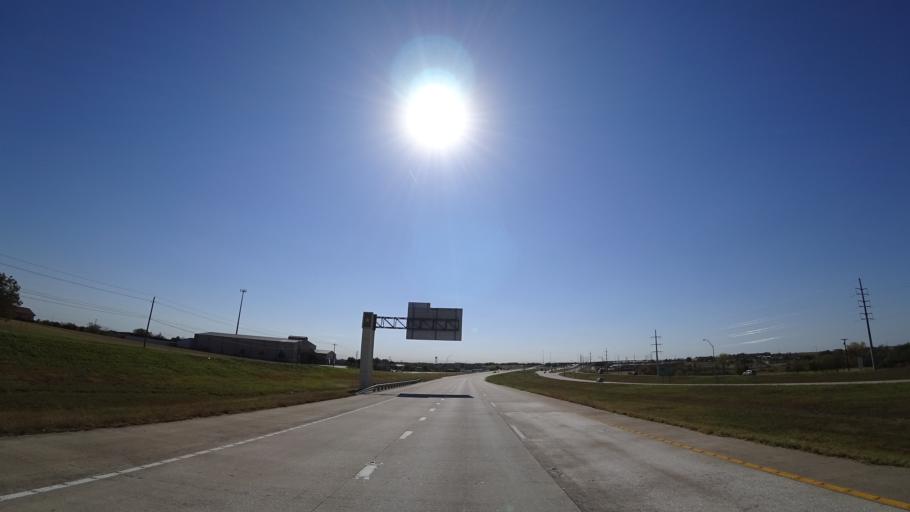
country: US
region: Texas
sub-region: Travis County
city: Pflugerville
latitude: 30.4875
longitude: -97.5841
